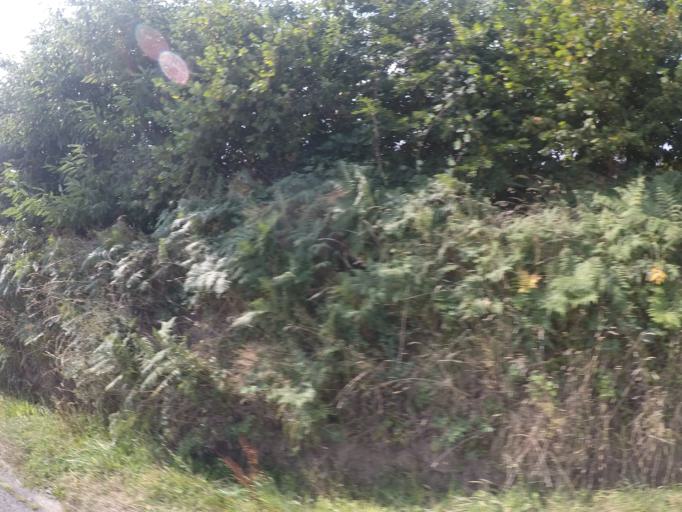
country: FR
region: Brittany
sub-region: Departement des Cotes-d'Armor
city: Tremuson
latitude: 48.5369
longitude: -2.8927
